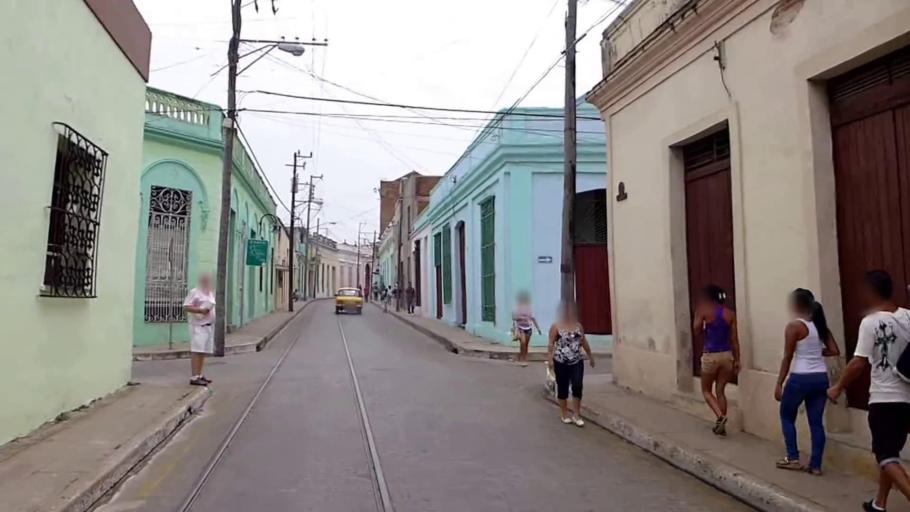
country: CU
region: Camaguey
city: Camaguey
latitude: 21.3773
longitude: -77.9173
